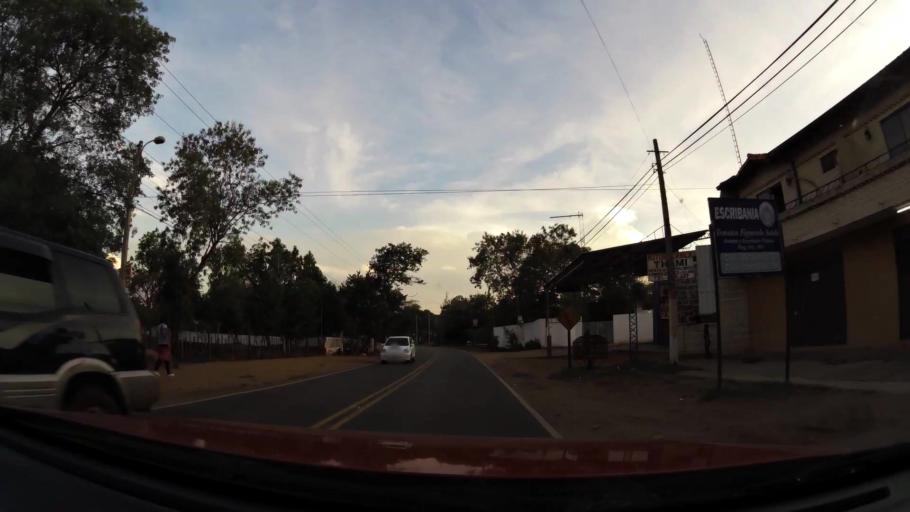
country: PY
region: Central
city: San Lorenzo
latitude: -25.3585
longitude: -57.4909
